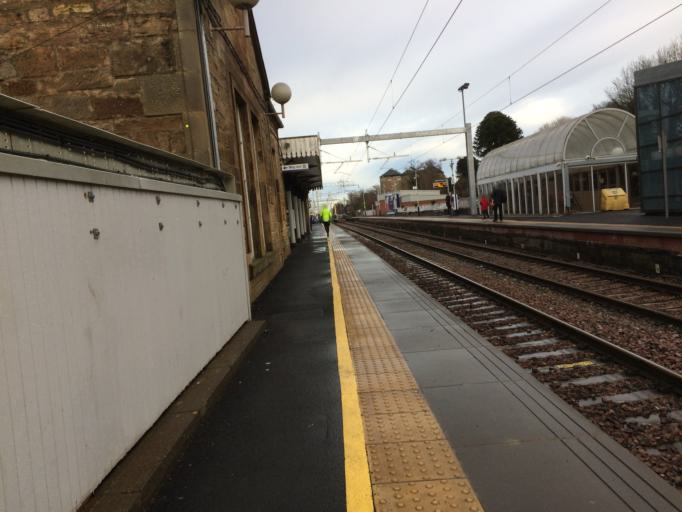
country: GB
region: Scotland
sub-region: West Lothian
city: Linlithgow
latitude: 55.9763
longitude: -3.5961
